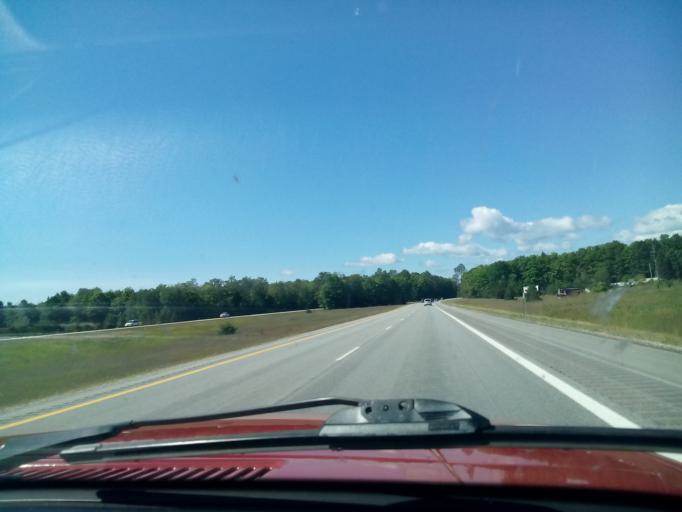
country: US
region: Michigan
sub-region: Cheboygan County
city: Indian River
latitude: 45.3210
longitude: -84.5991
